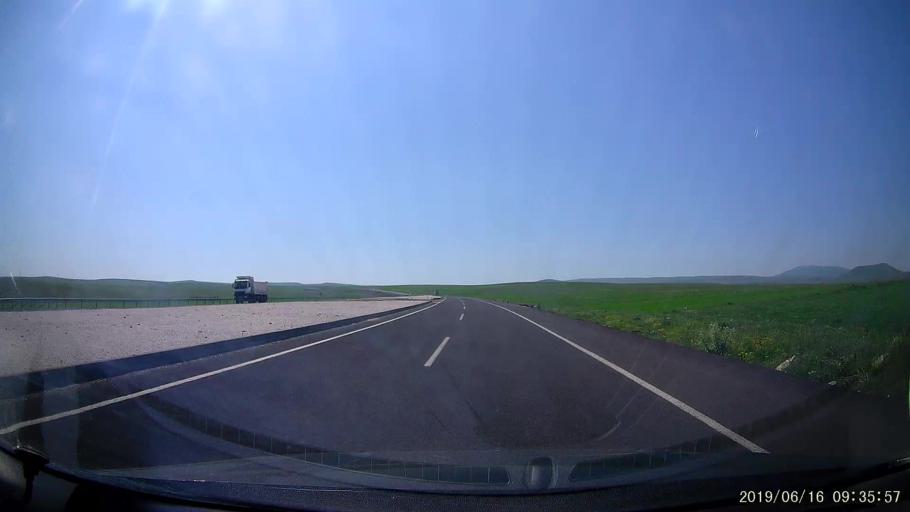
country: TR
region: Kars
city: Kars
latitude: 40.5638
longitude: 43.1645
